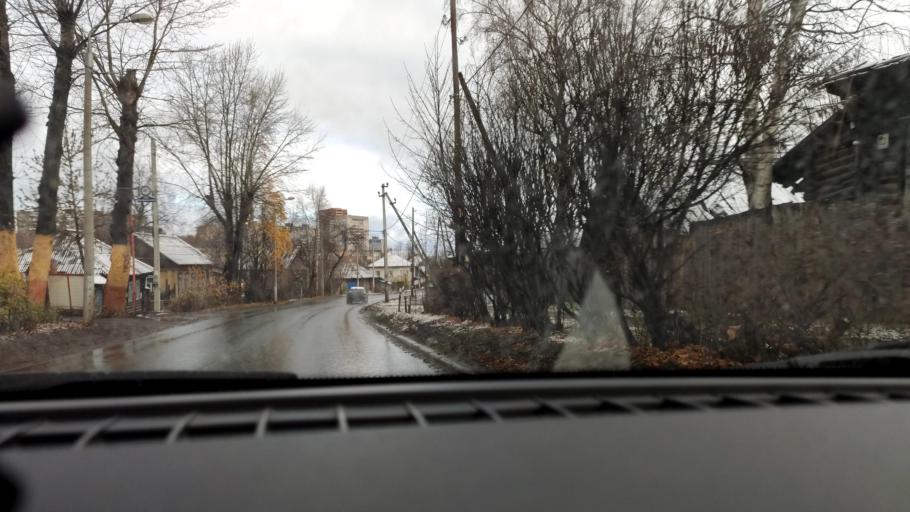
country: RU
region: Perm
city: Perm
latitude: 58.0231
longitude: 56.3126
